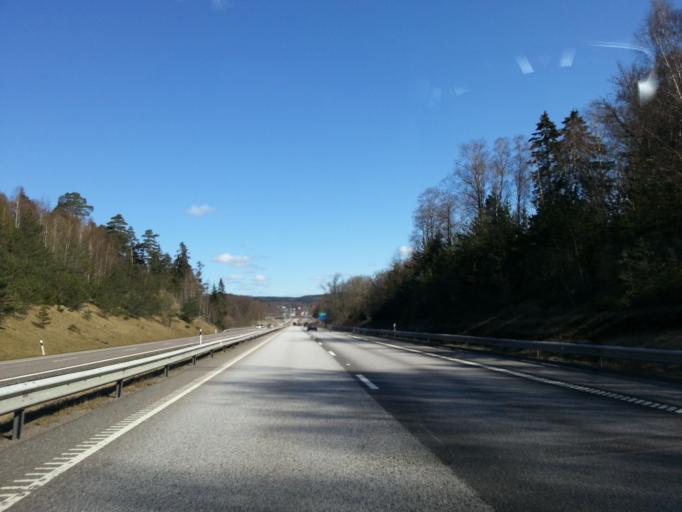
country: SE
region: Vaestra Goetaland
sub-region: Uddevalla Kommun
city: Ljungskile
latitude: 58.2057
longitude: 11.9106
